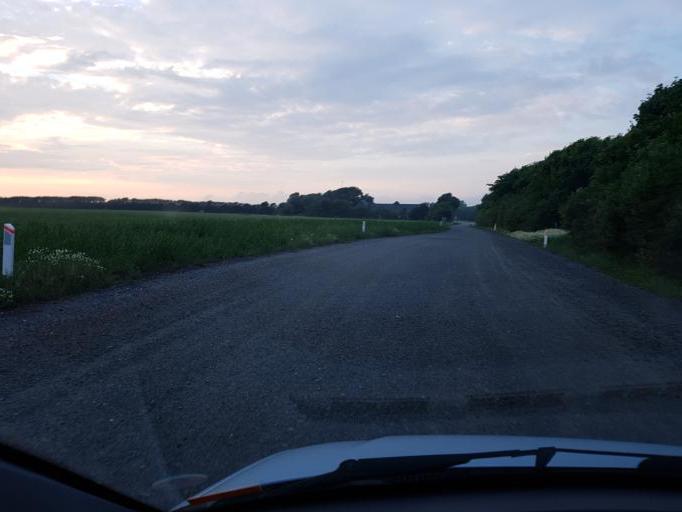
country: DK
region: South Denmark
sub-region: Esbjerg Kommune
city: Tjaereborg
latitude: 55.5009
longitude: 8.5544
